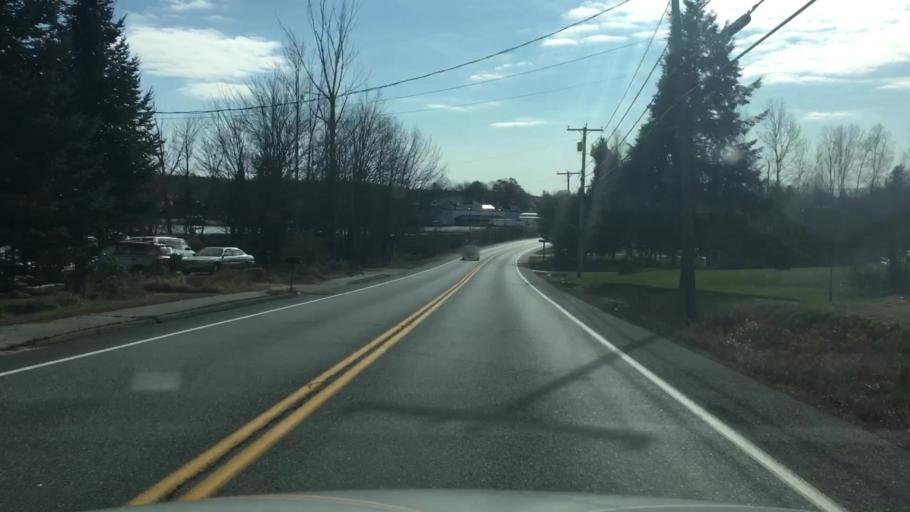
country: US
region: Maine
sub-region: Kennebec County
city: Winthrop
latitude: 44.3116
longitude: -69.9773
